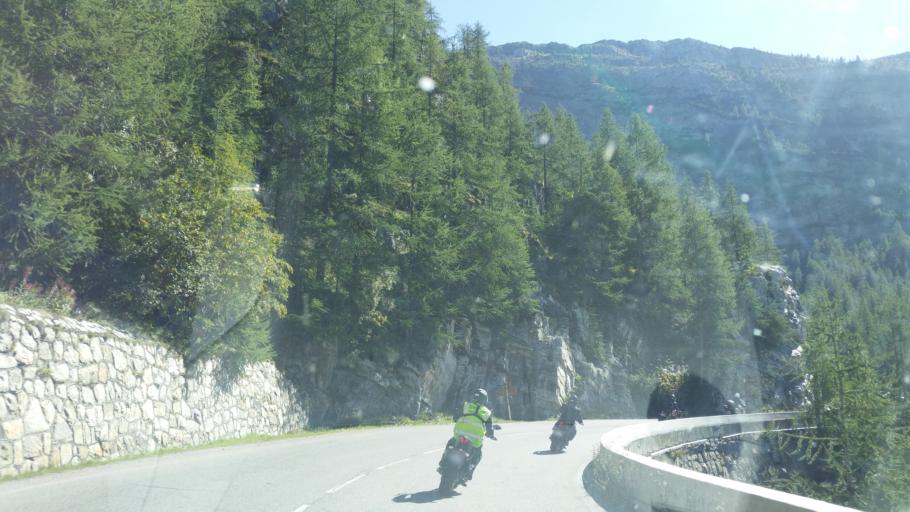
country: FR
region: Rhone-Alpes
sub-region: Departement de la Savoie
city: Tignes
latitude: 45.4754
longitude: 6.9492
